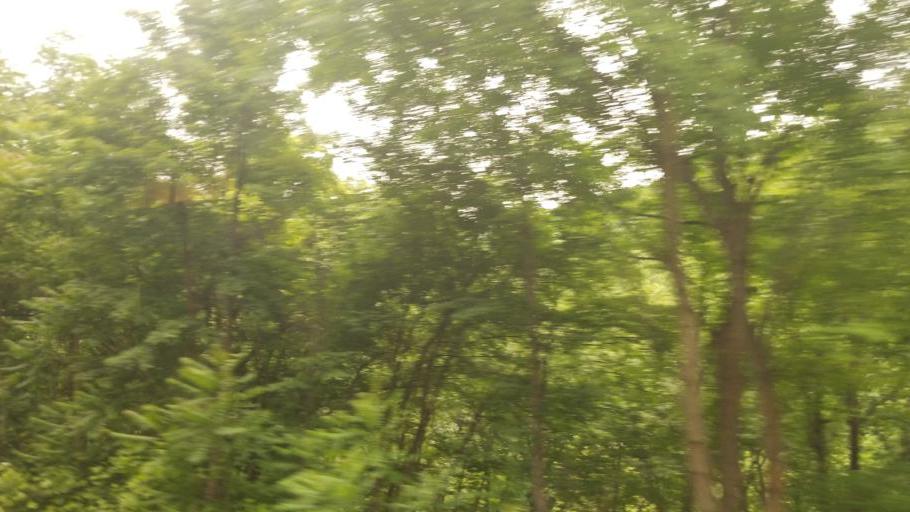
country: US
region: Pennsylvania
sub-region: Fayette County
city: South Connellsville
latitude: 39.9285
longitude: -79.4867
